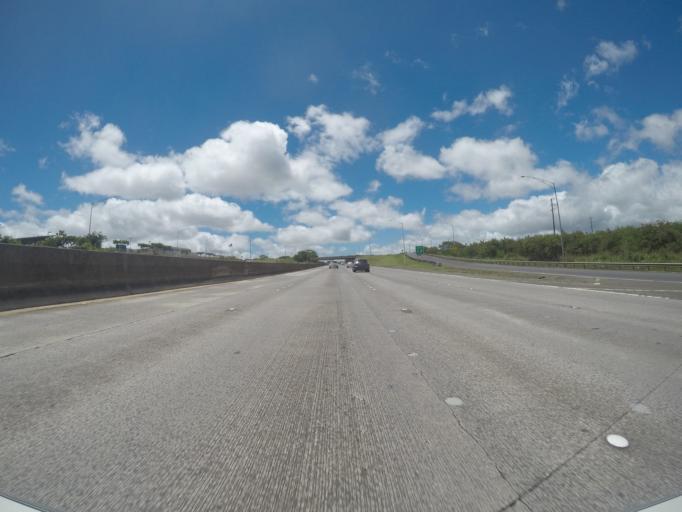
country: US
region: Hawaii
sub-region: Honolulu County
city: Waipio
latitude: 21.4258
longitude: -157.9957
